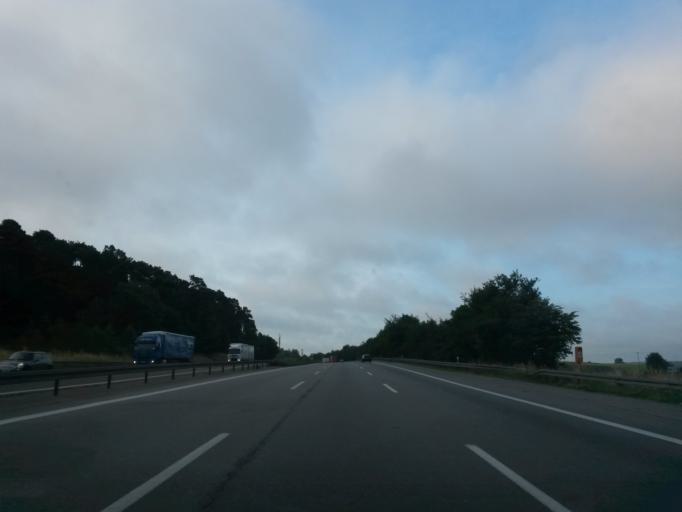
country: DE
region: Bavaria
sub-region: Upper Bavaria
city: Rohrbach
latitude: 48.6284
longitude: 11.5246
